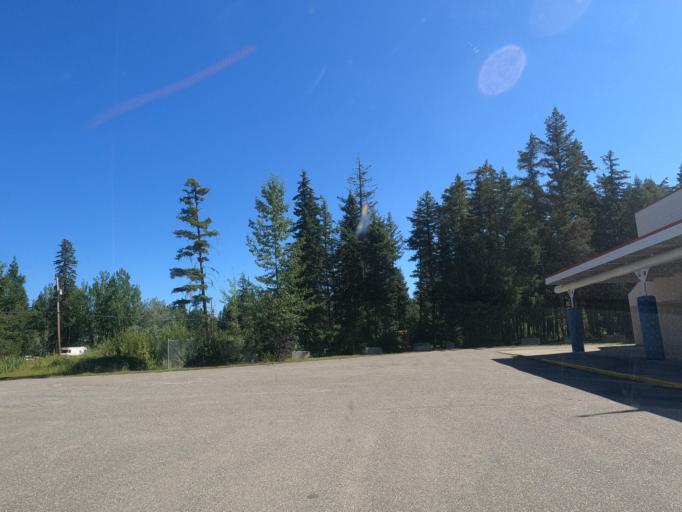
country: CA
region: British Columbia
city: Quesnel
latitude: 53.0207
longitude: -122.4547
